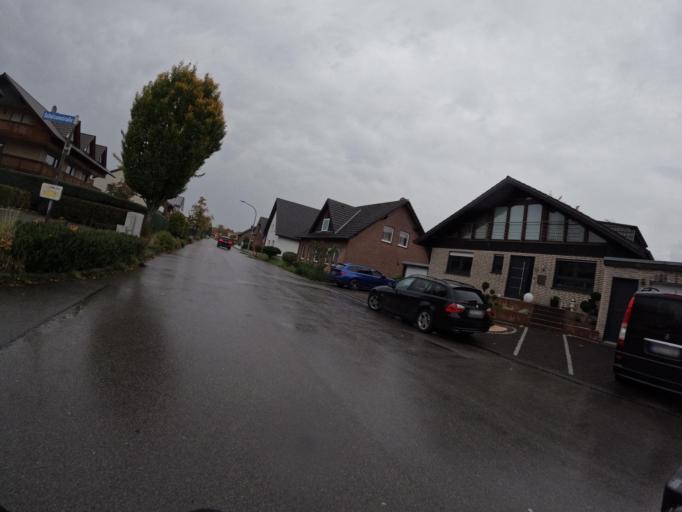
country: DE
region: North Rhine-Westphalia
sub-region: Regierungsbezirk Detmold
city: Hovelhof
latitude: 51.8189
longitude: 8.6633
